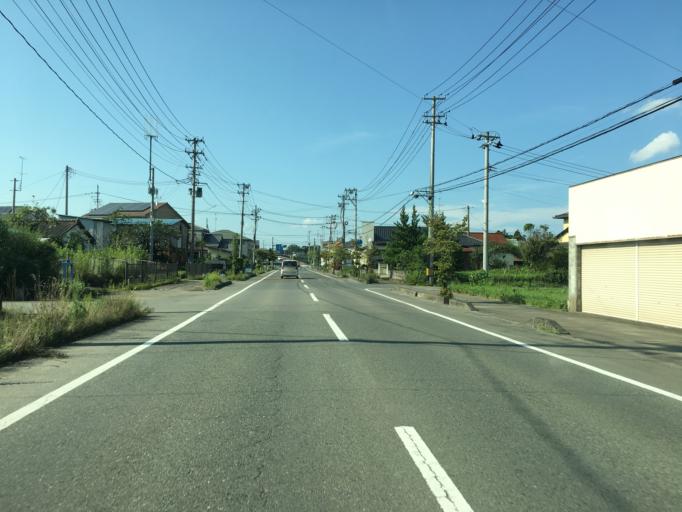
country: JP
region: Miyagi
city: Marumori
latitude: 37.7877
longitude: 140.9135
